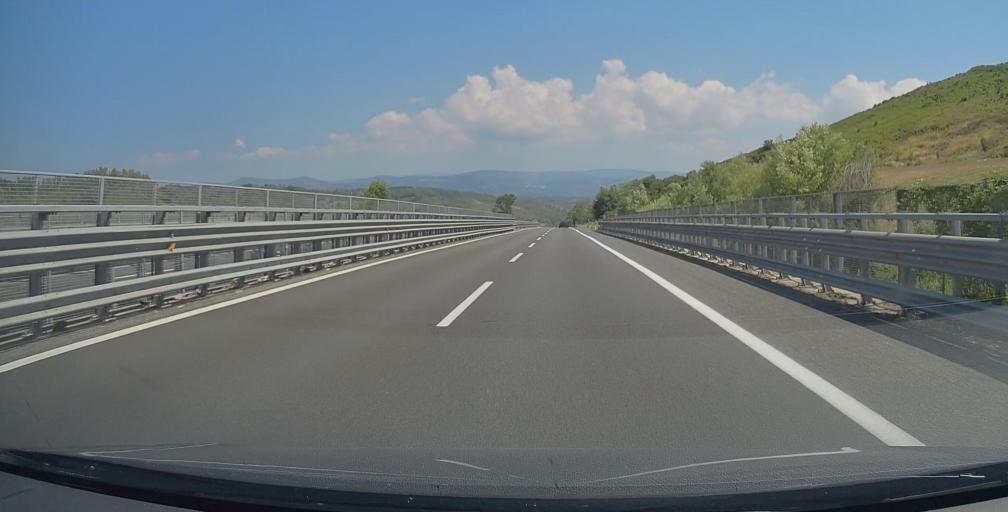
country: IT
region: Calabria
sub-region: Provincia di Vibo-Valentia
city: Maierato
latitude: 38.6758
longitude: 16.1768
